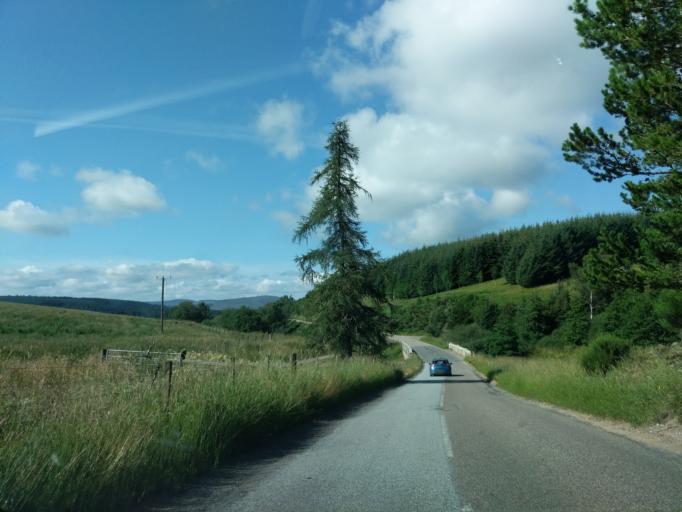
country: GB
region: Scotland
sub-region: Moray
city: Dufftown
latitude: 57.3725
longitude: -3.2500
